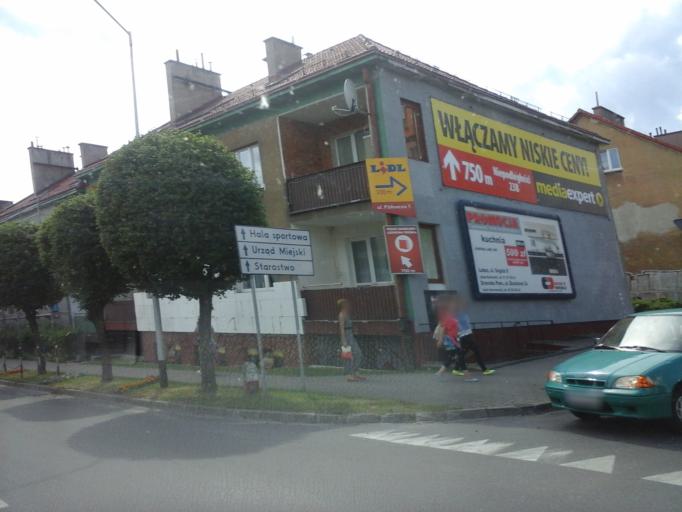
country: PL
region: West Pomeranian Voivodeship
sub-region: Powiat lobeski
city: Lobez
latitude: 53.6392
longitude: 15.6213
